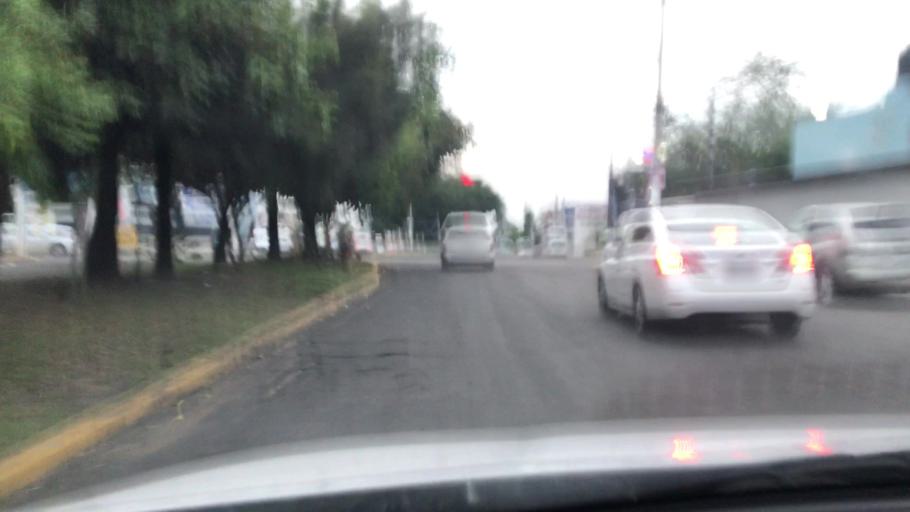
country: MX
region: Jalisco
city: Guadalajara
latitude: 20.6466
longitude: -103.4280
